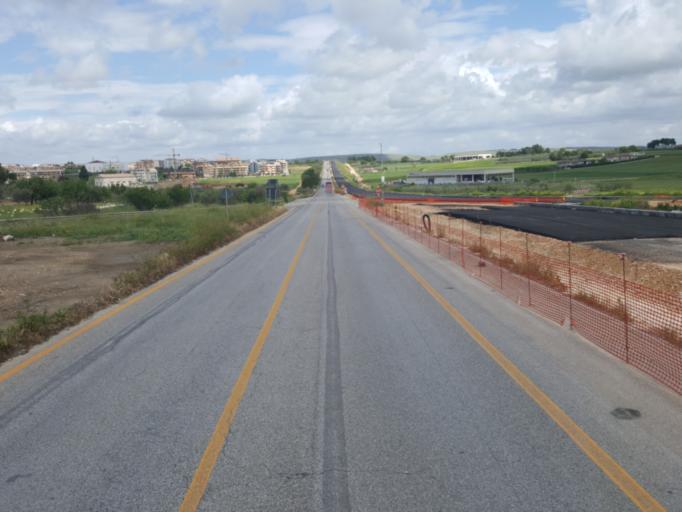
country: IT
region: Apulia
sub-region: Provincia di Bari
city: Altamura
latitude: 40.8248
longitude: 16.5707
